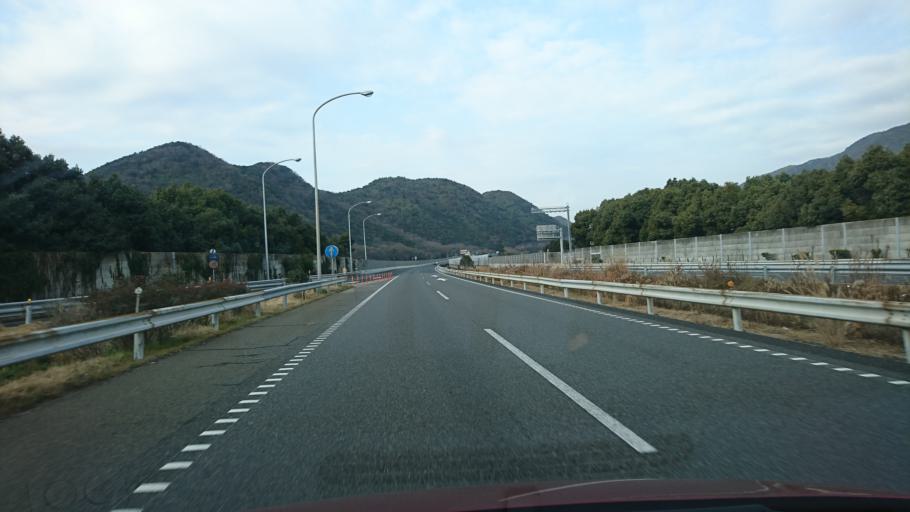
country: JP
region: Hyogo
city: Kariya
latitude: 34.7737
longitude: 134.3728
